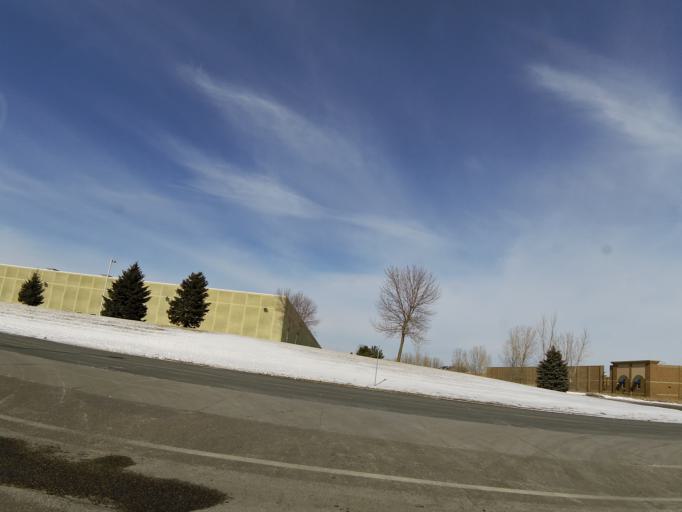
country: US
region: Minnesota
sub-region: Washington County
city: Woodbury
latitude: 44.9414
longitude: -92.9087
